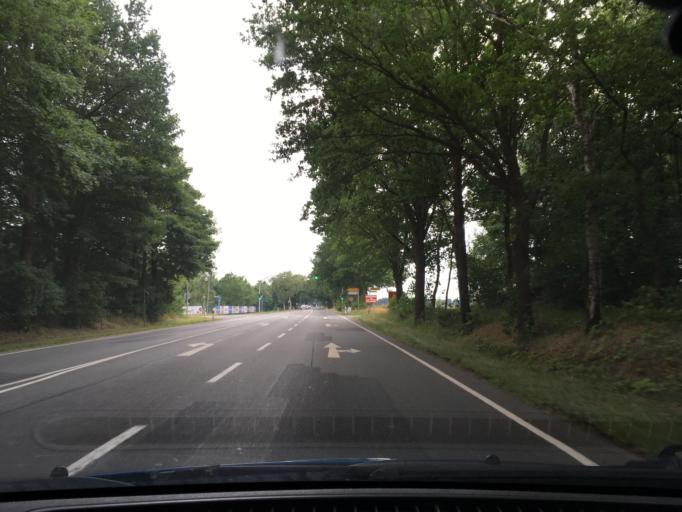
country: DE
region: Lower Saxony
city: Tostedt
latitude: 53.2949
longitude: 9.7364
